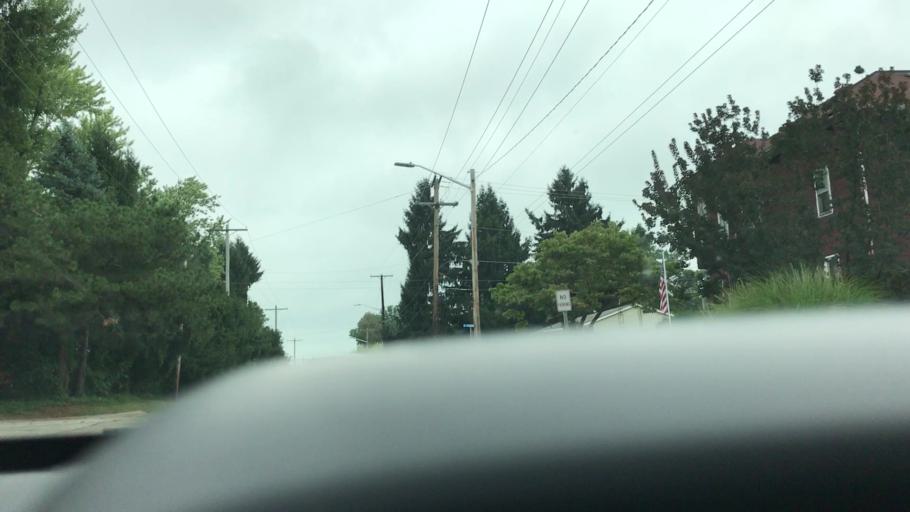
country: US
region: Ohio
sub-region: Stark County
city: Brewster
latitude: 40.7214
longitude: -81.5971
